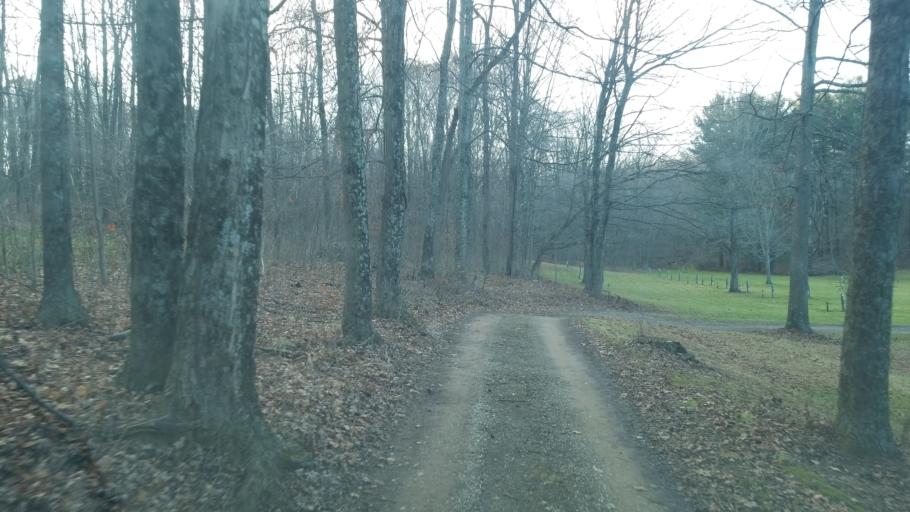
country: US
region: Ohio
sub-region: Sandusky County
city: Bellville
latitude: 40.5921
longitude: -82.5552
